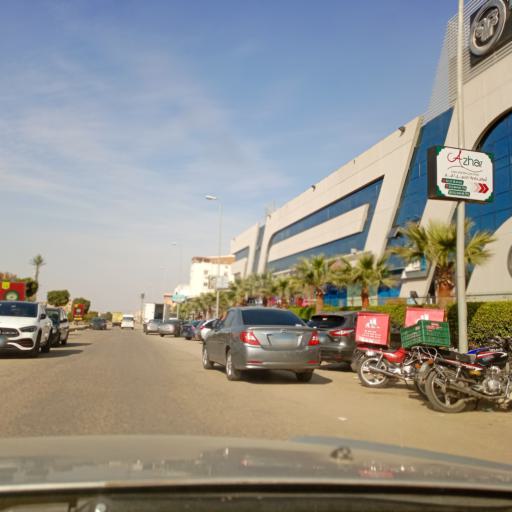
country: EG
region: Muhafazat al Qalyubiyah
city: Al Khankah
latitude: 30.0348
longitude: 31.4857
